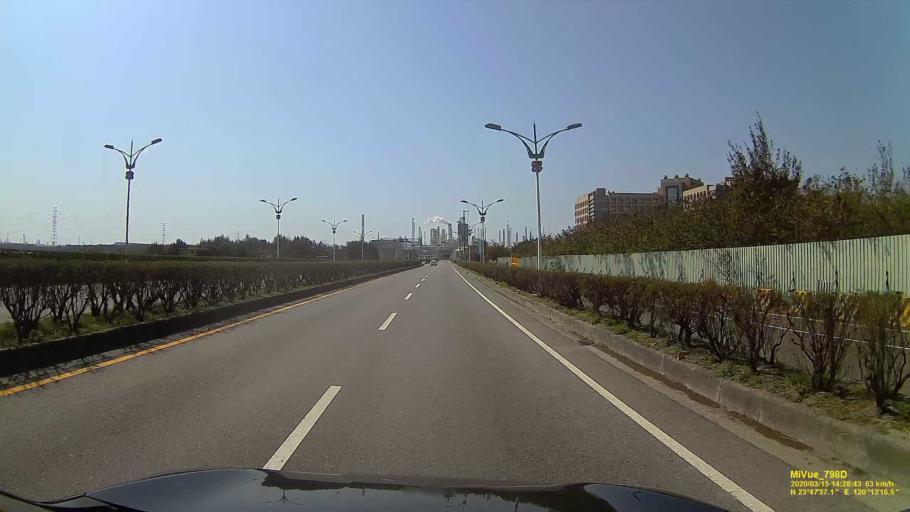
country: TW
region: Taiwan
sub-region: Yunlin
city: Douliu
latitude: 23.7939
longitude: 120.2209
